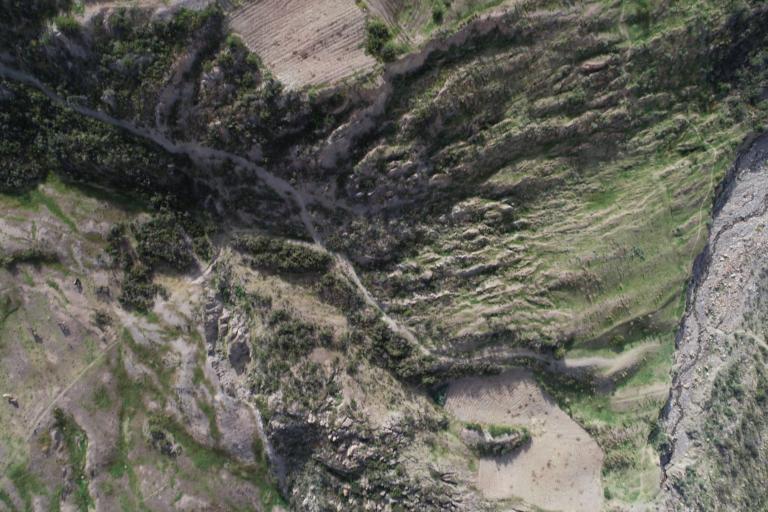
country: BO
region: La Paz
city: La Paz
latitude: -16.5503
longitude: -67.9959
